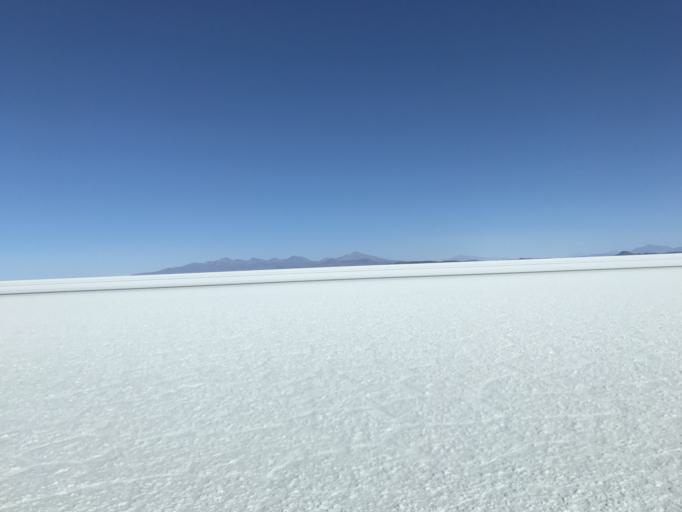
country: BO
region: Potosi
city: Colchani
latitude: -20.2395
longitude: -67.6139
